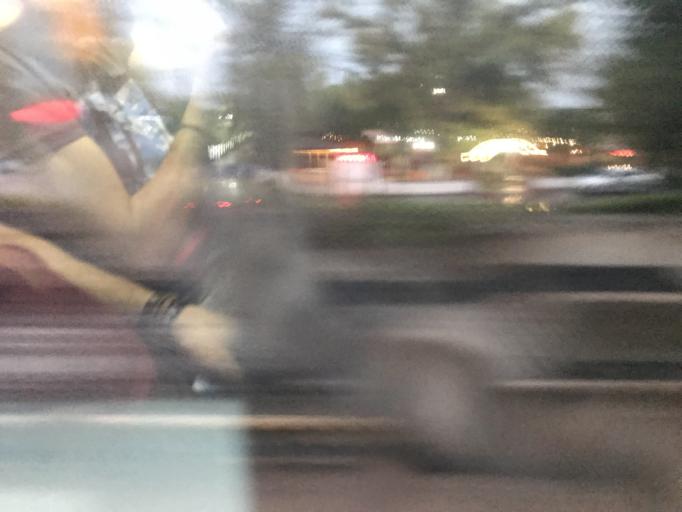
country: TR
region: Kocaeli
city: Hereke
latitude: 40.7841
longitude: 29.6172
